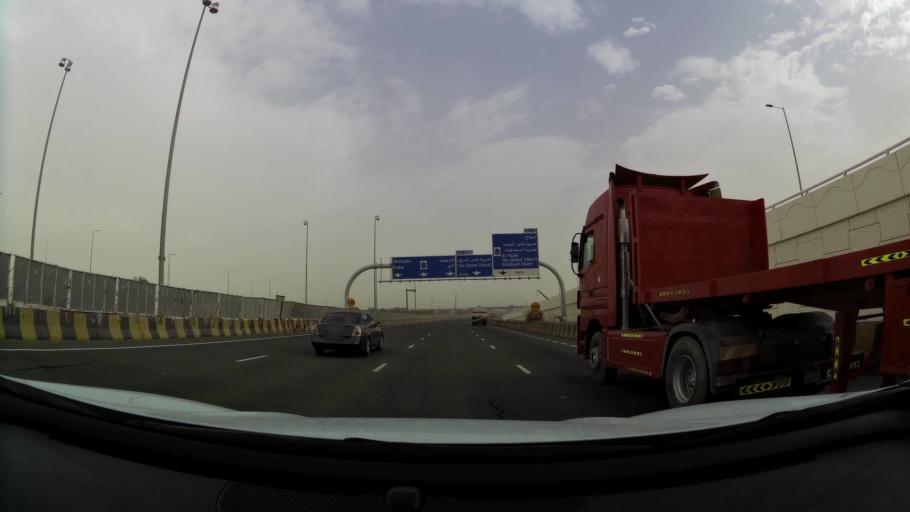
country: AE
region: Abu Dhabi
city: Abu Dhabi
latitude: 24.4669
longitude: 54.6305
